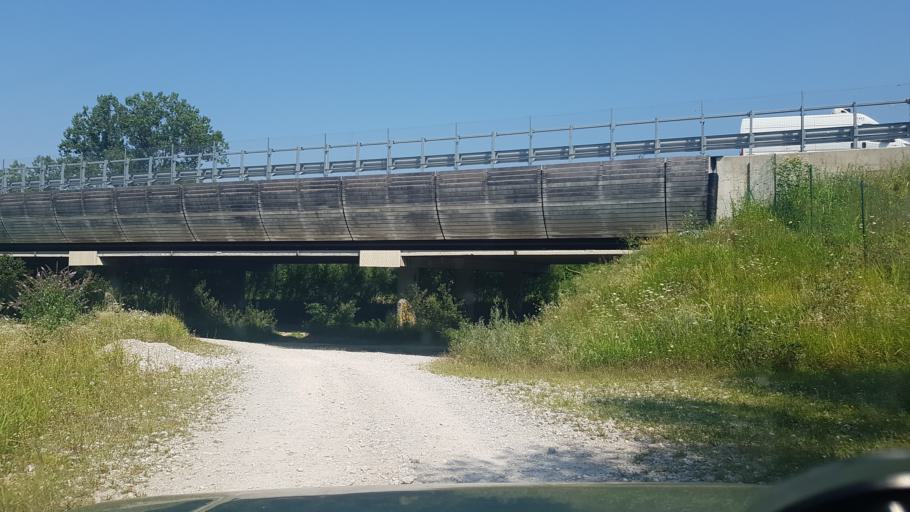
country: IT
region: Friuli Venezia Giulia
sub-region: Provincia di Gorizia
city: Savogna d'Isonzo
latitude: 45.9035
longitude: 13.5597
